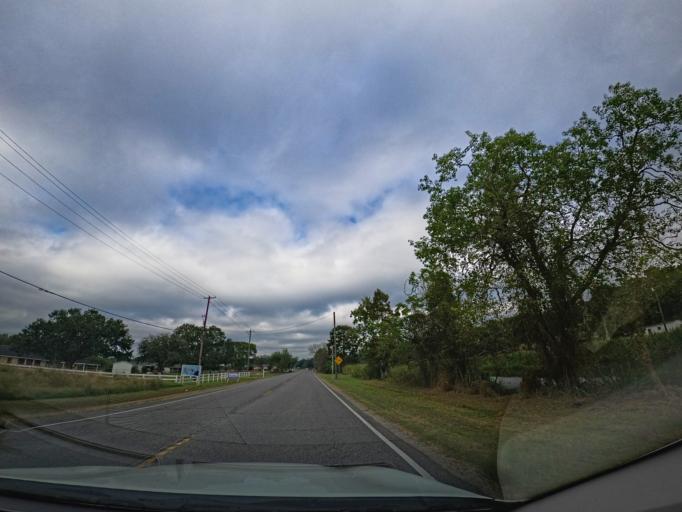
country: US
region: Louisiana
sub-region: Saint Mary Parish
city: Amelia
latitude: 29.6401
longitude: -90.9566
